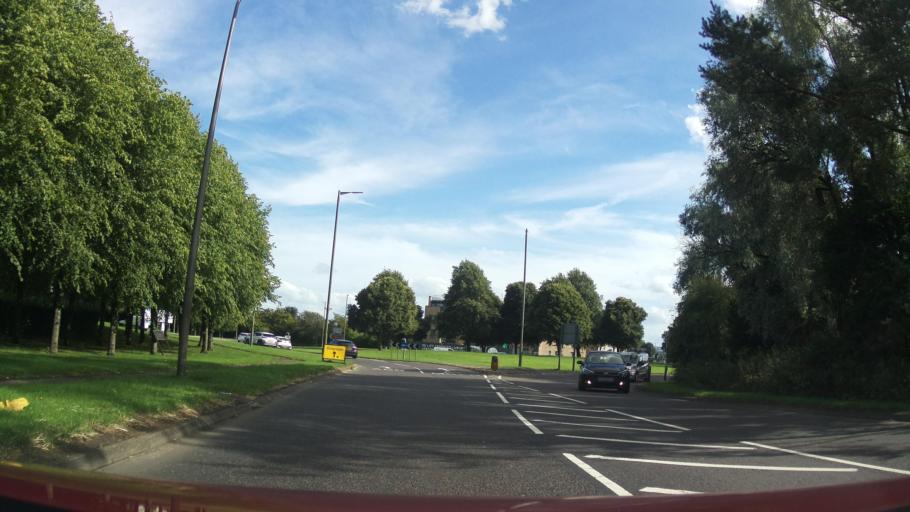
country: GB
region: Scotland
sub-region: Falkirk
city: Larbert
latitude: 56.0306
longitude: -3.8460
